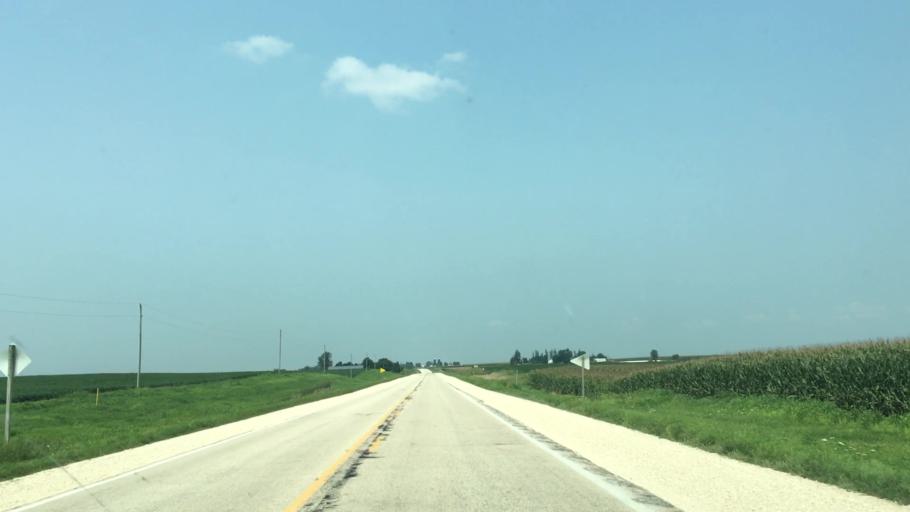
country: US
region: Iowa
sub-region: Fayette County
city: West Union
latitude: 42.9849
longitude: -91.8242
